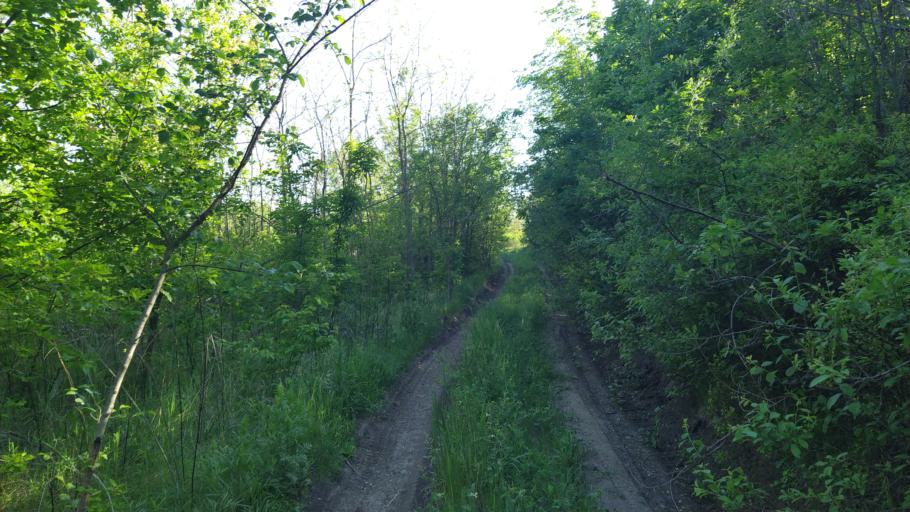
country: RU
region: Rostov
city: Bataysk
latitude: 47.0768
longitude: 39.7174
